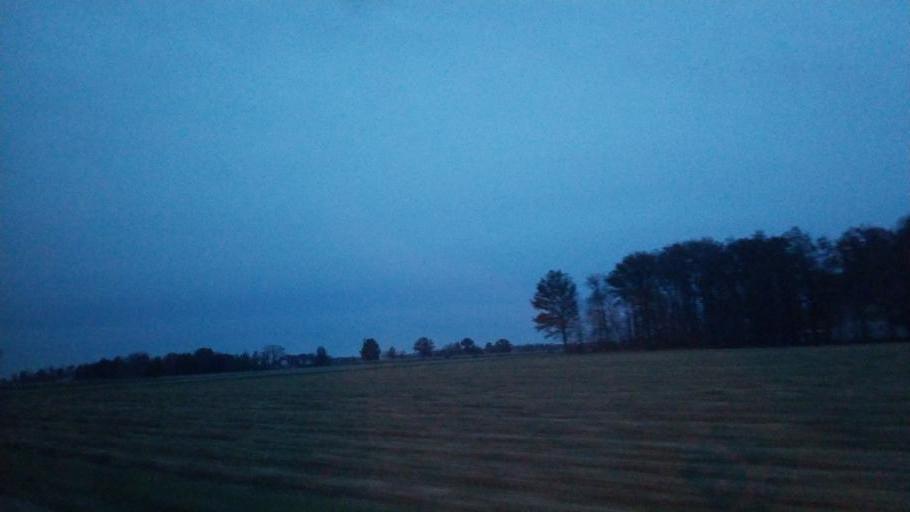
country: US
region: Indiana
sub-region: Adams County
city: Berne
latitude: 40.7072
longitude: -84.9940
